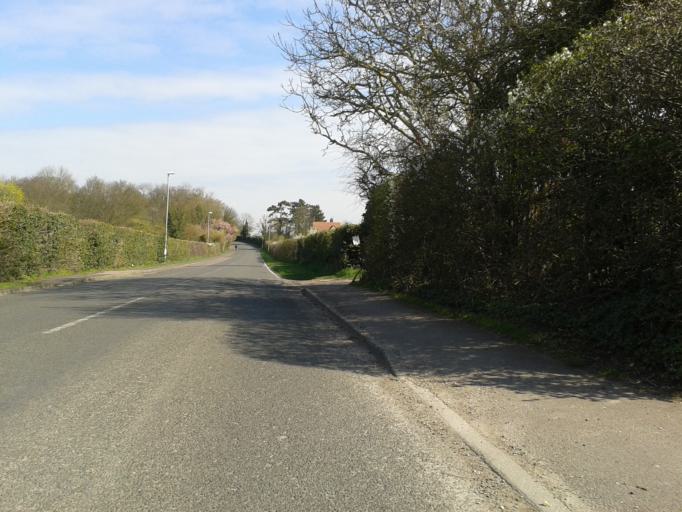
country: GB
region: England
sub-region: Cambridgeshire
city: Sawston
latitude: 52.1557
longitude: 0.1514
